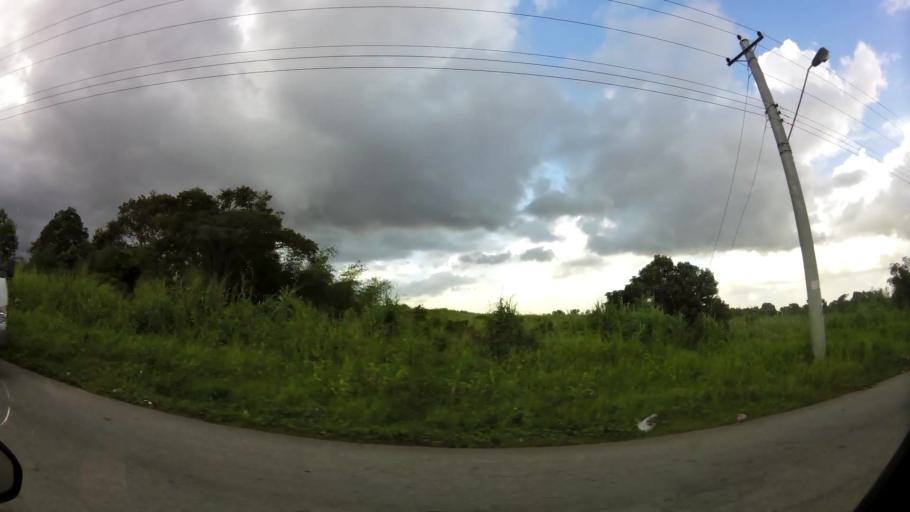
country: TT
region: City of San Fernando
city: Mon Repos
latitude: 10.2557
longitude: -61.4343
